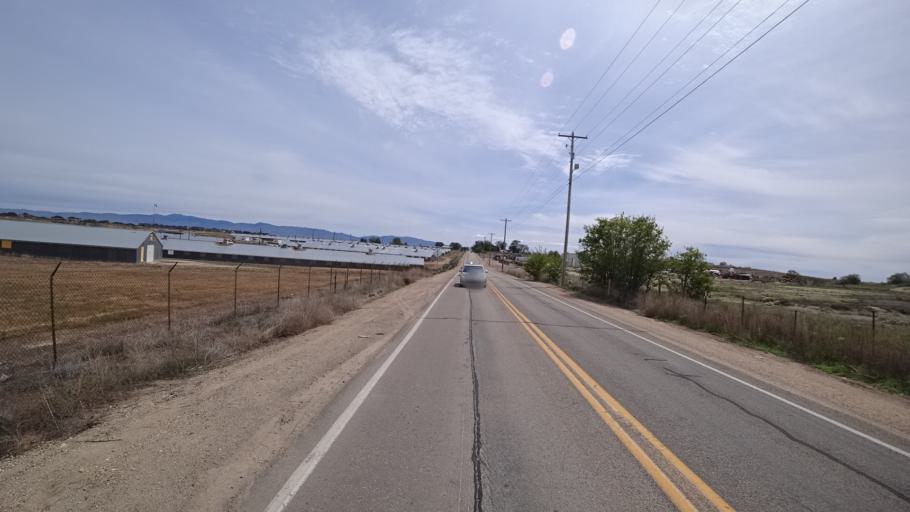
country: US
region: Idaho
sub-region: Ada County
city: Meridian
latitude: 43.5610
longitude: -116.3920
